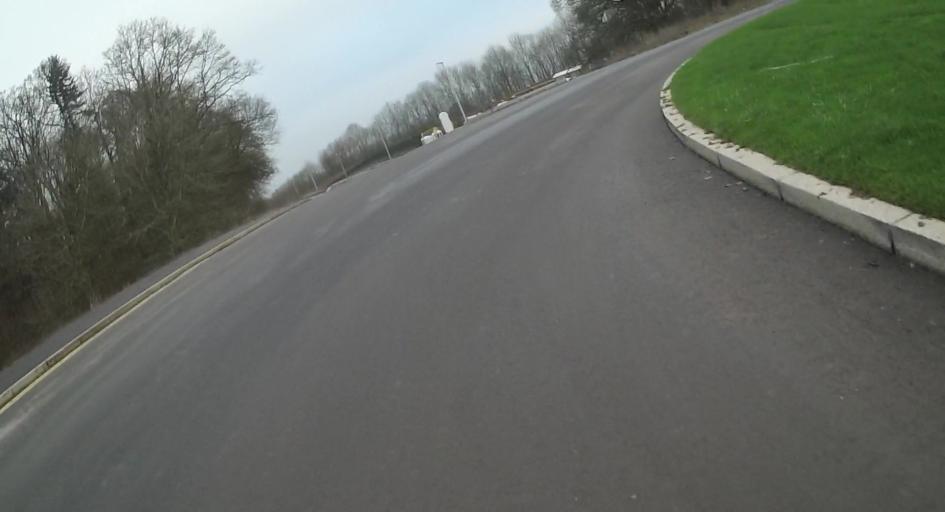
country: GB
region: England
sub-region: Wokingham
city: Wokingham
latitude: 51.4169
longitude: -0.8100
